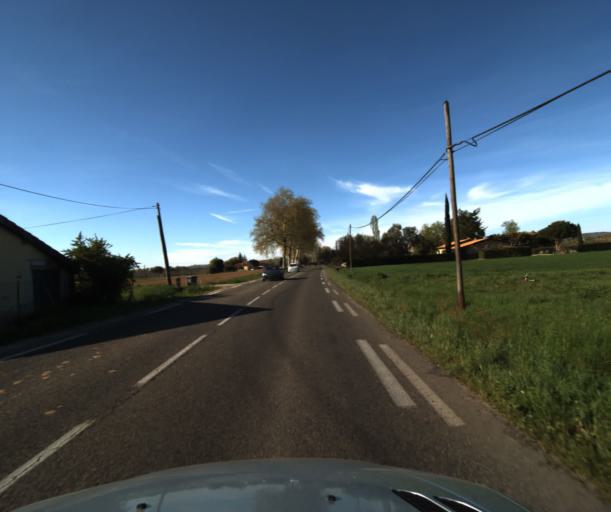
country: FR
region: Midi-Pyrenees
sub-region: Departement du Tarn-et-Garonne
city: Montbeton
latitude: 44.0650
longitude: 1.2872
